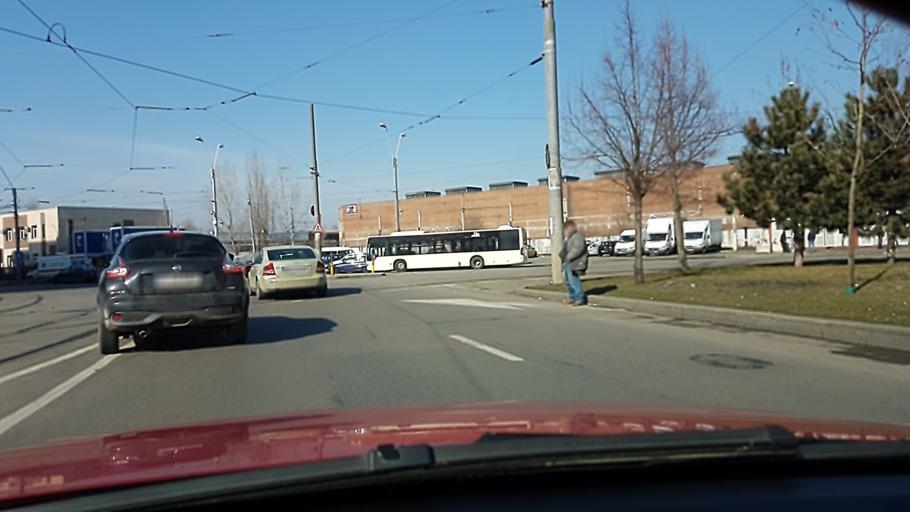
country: RO
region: Ilfov
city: Dobroesti
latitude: 44.4269
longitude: 26.1791
